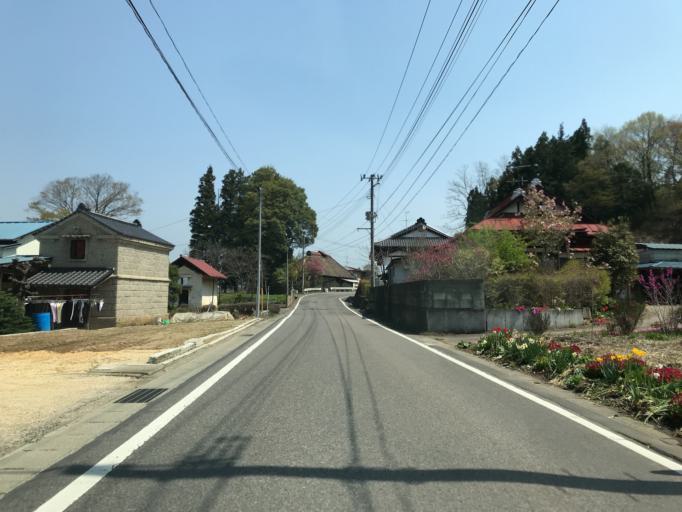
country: JP
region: Fukushima
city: Ishikawa
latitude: 37.1103
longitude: 140.3700
